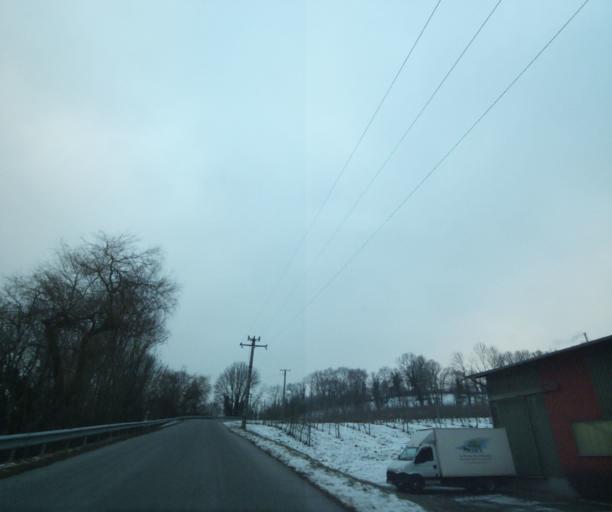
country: FR
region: Rhone-Alpes
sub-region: Departement de la Haute-Savoie
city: Vetraz-Monthoux
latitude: 46.1582
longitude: 6.2432
